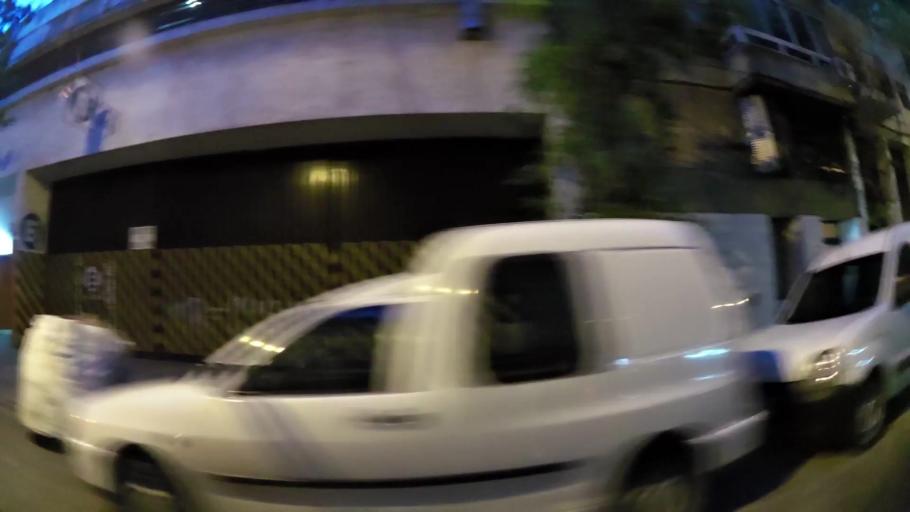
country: AR
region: Santa Fe
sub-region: Departamento de Rosario
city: Rosario
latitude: -32.9522
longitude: -60.6526
